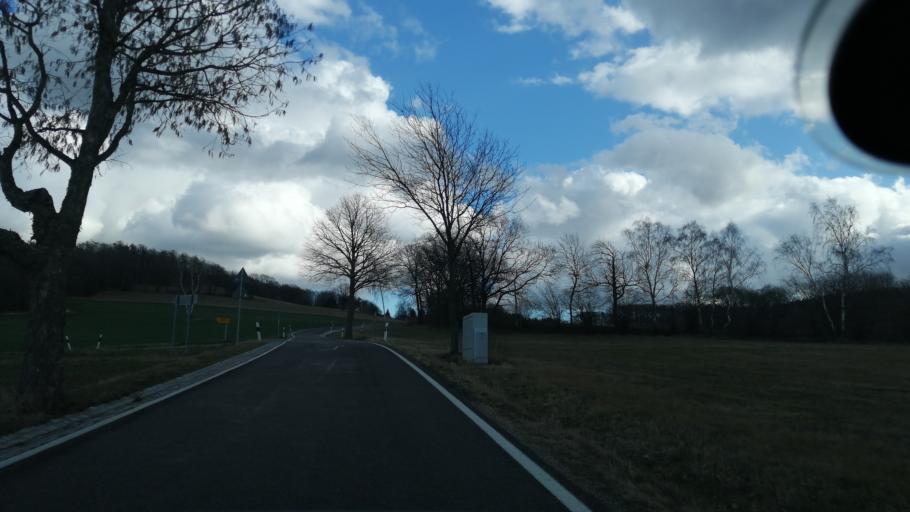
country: DE
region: Saxony
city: Grosspostwitz
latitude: 51.1427
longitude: 14.4694
